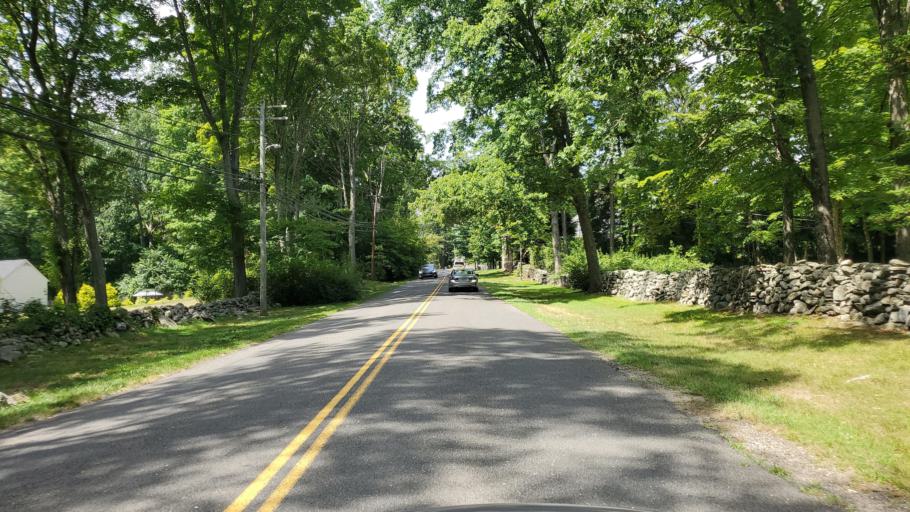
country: US
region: Connecticut
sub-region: Fairfield County
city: Westport
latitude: 41.2113
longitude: -73.3182
